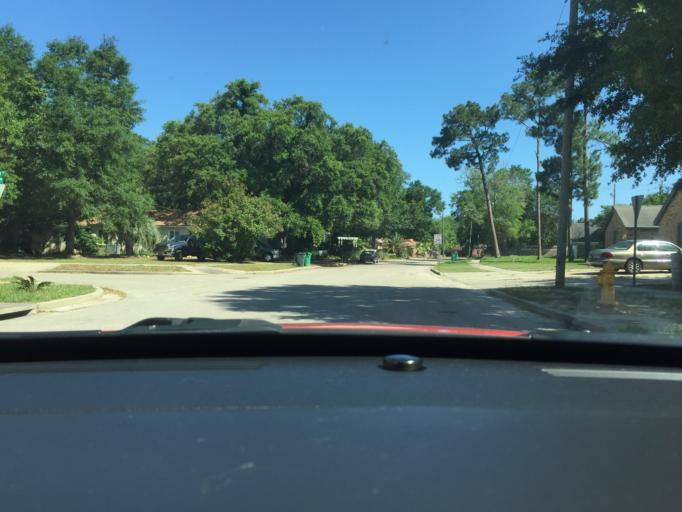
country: US
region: Mississippi
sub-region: Harrison County
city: D'Iberville
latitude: 30.3933
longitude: -88.9880
